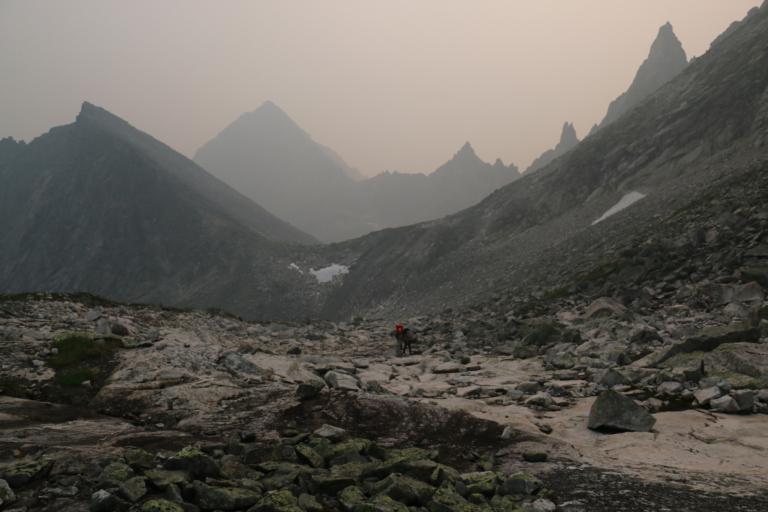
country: RU
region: Respublika Buryatiya
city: Kichera
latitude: 56.2287
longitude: 110.8659
